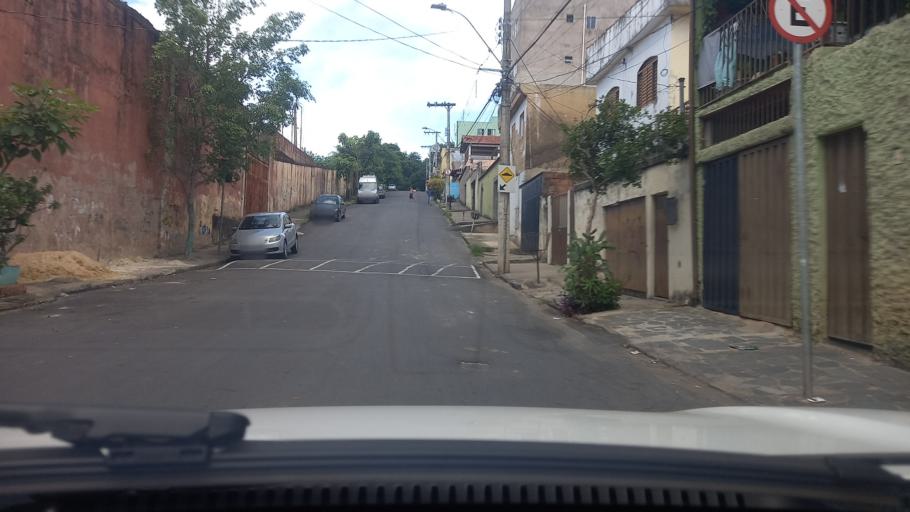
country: BR
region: Minas Gerais
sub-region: Belo Horizonte
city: Belo Horizonte
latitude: -19.8598
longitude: -43.9209
